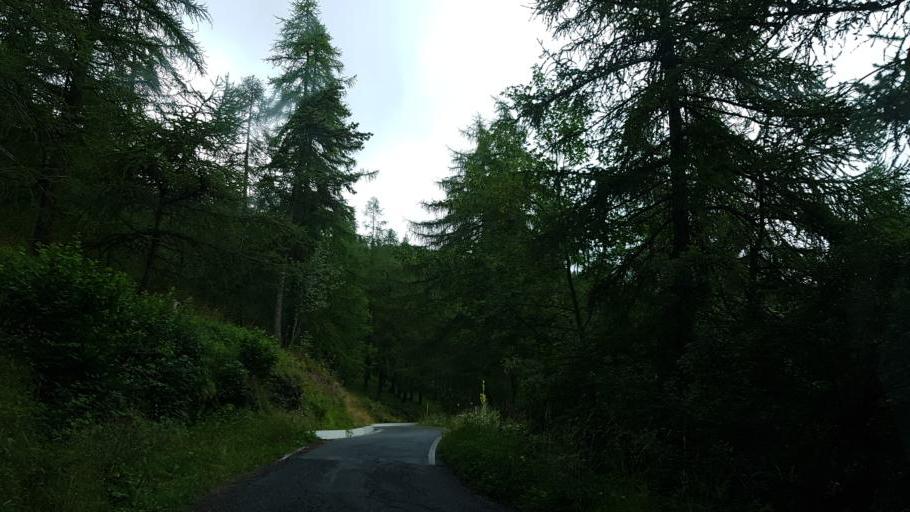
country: IT
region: Piedmont
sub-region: Provincia di Cuneo
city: Stroppo
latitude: 44.5126
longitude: 7.1083
